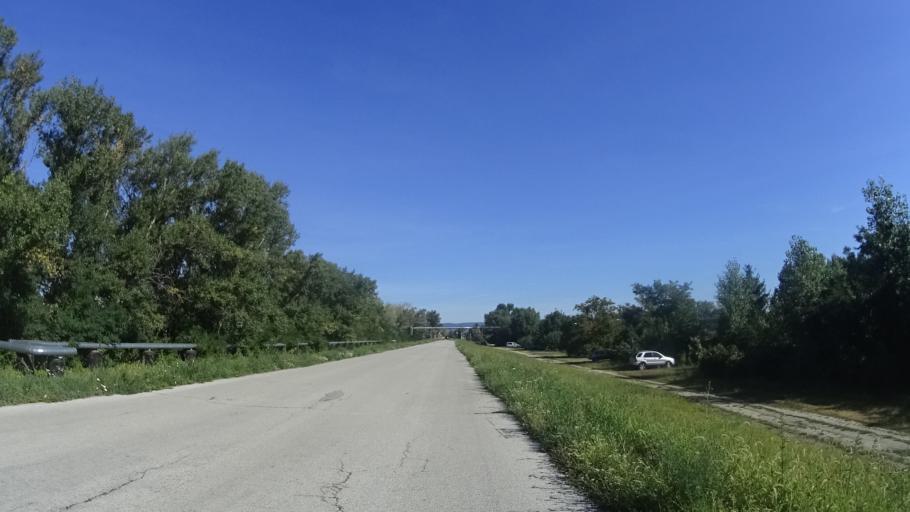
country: SK
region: Bratislavsky
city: Bratislava
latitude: 48.1264
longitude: 17.1593
